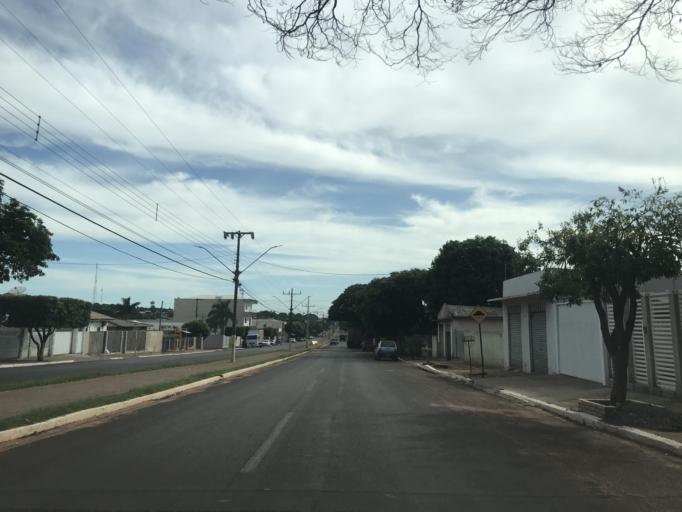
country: BR
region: Parana
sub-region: Paranavai
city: Nova Aurora
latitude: -22.9417
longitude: -52.6908
